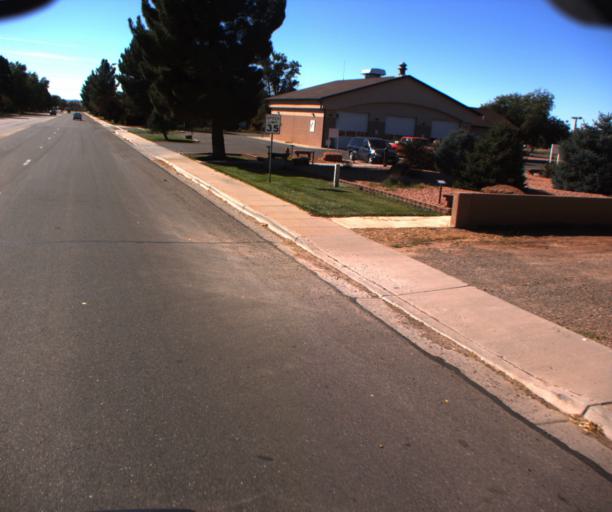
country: US
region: Arizona
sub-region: Coconino County
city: Fredonia
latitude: 36.9500
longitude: -112.5265
